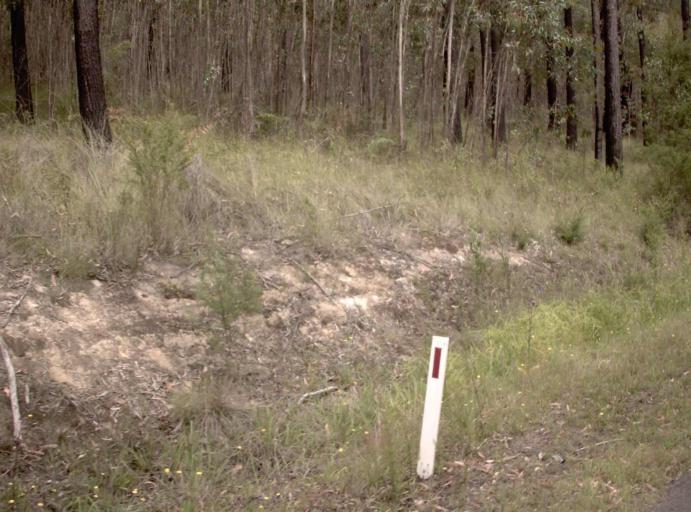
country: AU
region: Victoria
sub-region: Latrobe
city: Morwell
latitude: -38.0789
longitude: 146.4295
